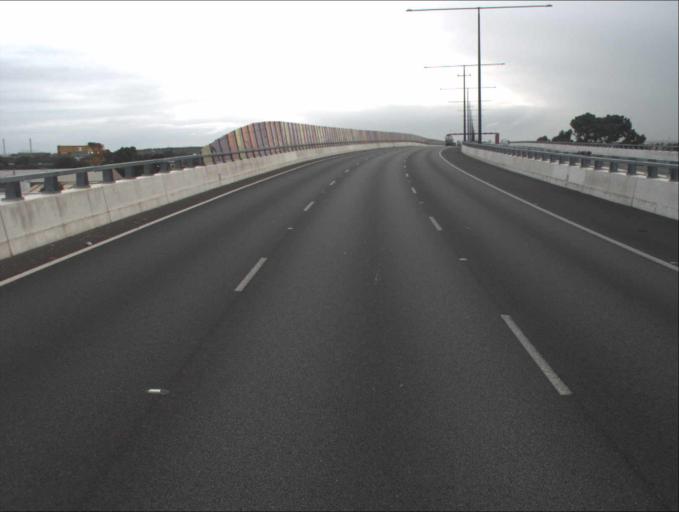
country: AU
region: South Australia
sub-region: Charles Sturt
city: Woodville North
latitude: -34.8570
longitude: 138.5651
